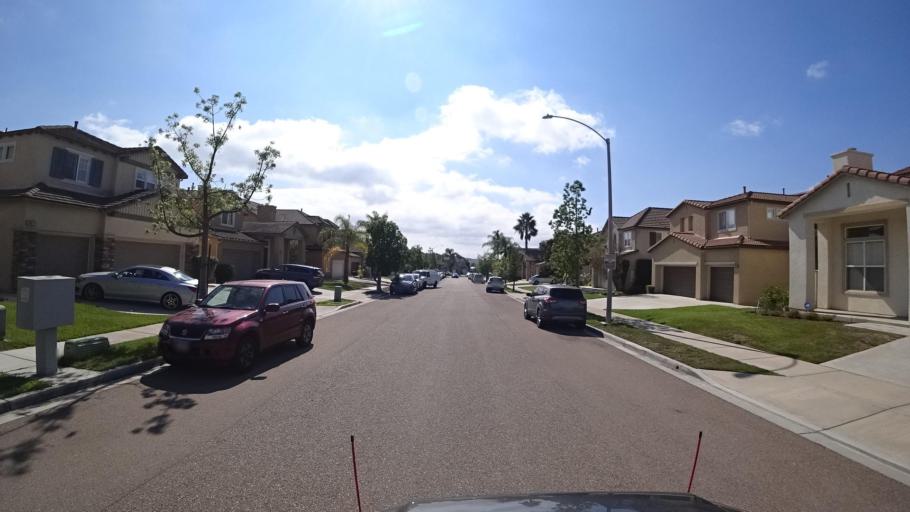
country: US
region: California
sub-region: San Diego County
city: Fairbanks Ranch
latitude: 33.0067
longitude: -117.1144
